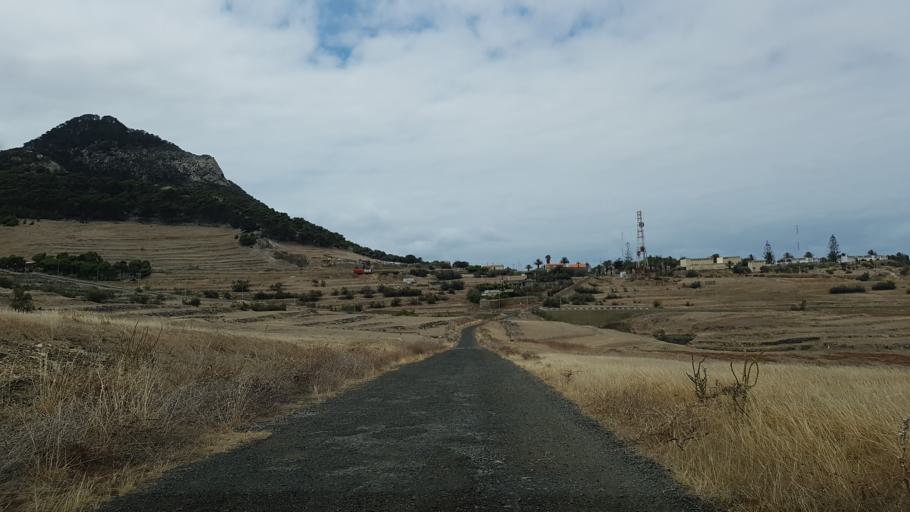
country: PT
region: Madeira
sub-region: Porto Santo
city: Camacha
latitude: 33.0912
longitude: -16.3360
